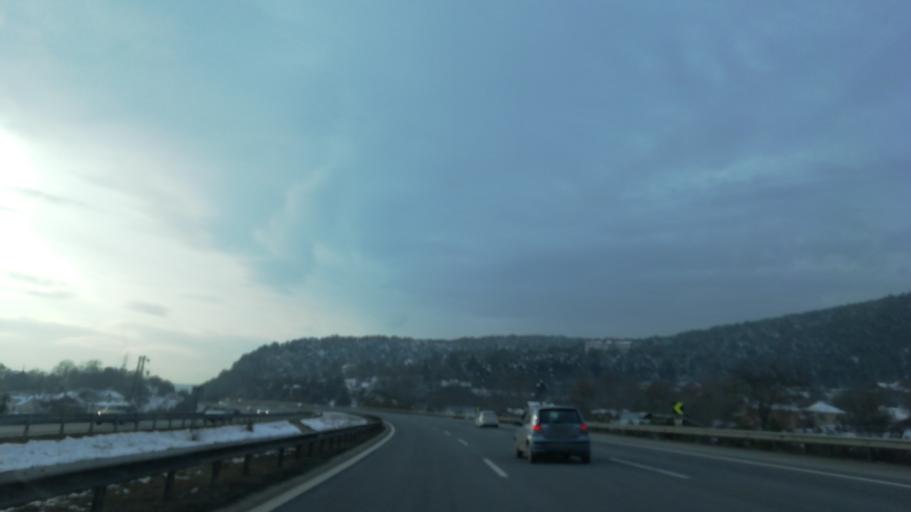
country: TR
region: Bolu
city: Bolu
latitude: 40.7612
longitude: 31.5889
